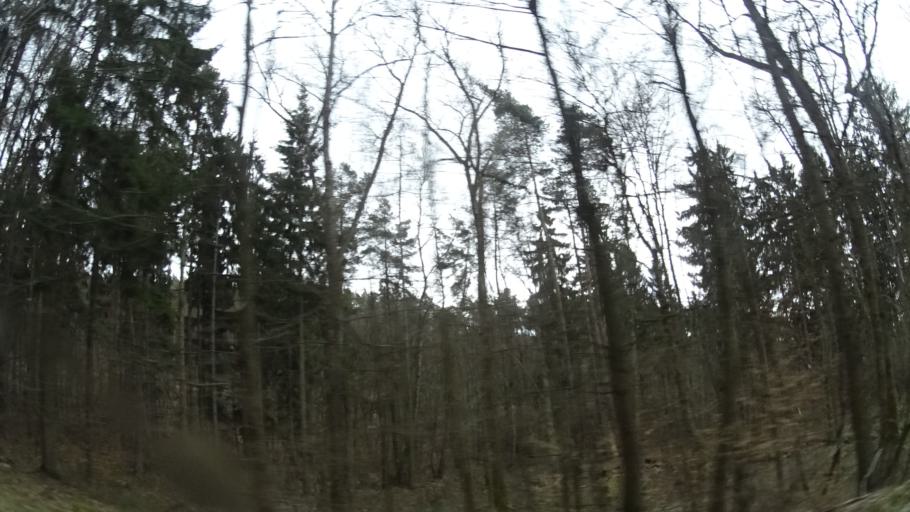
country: DE
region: Rheinland-Pfalz
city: Daxweiler
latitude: 49.9738
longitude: 7.7635
